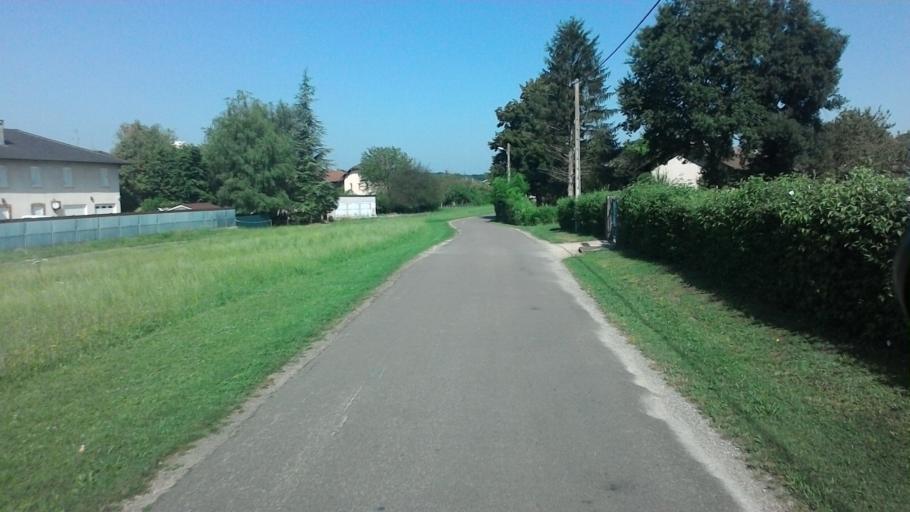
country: FR
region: Rhone-Alpes
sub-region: Departement de l'Ain
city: Saint-Trivier-de-Courtes
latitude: 46.4029
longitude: 5.1112
